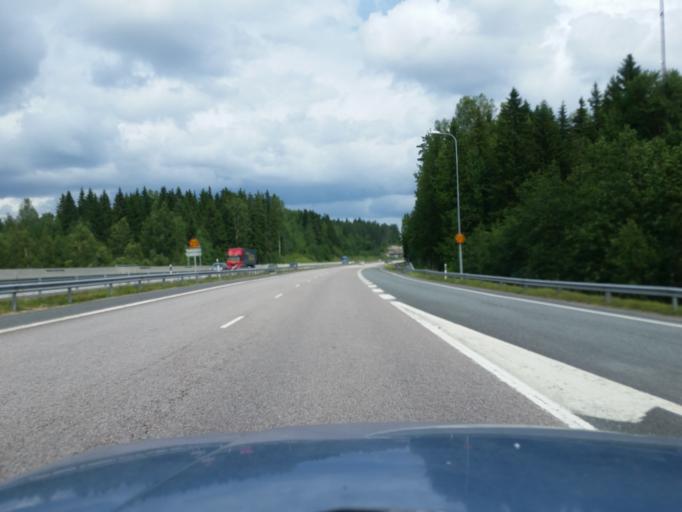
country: FI
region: Paijanne Tavastia
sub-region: Lahti
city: Lahti
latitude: 60.9995
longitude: 25.7893
